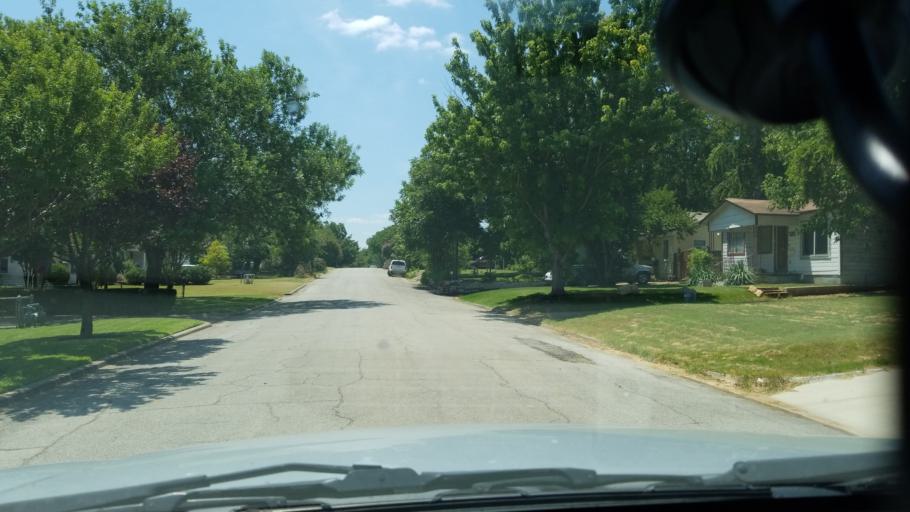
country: US
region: Texas
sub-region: Dallas County
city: Grand Prairie
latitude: 32.7555
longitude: -96.9570
